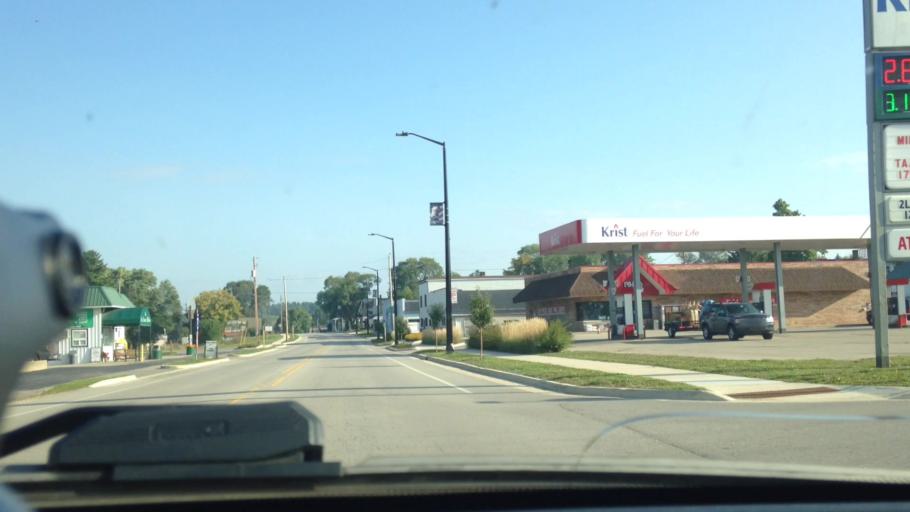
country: US
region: Wisconsin
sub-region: Marinette County
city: Peshtigo
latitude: 45.3705
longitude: -87.9523
